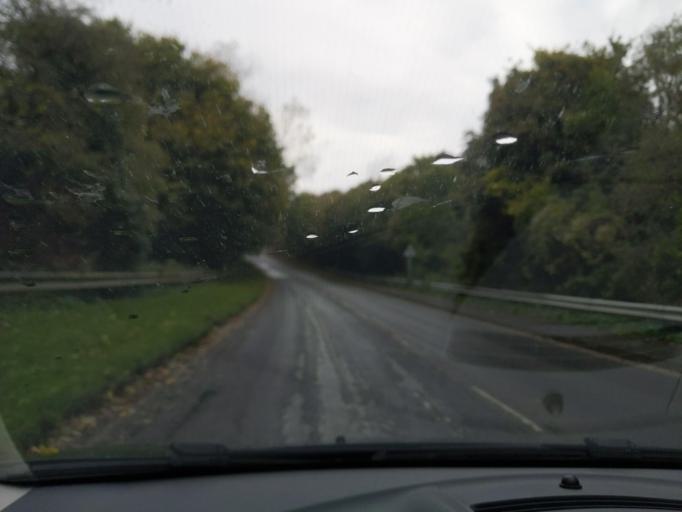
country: GB
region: England
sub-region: Cornwall
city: Padstow
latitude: 50.5401
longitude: -4.9436
